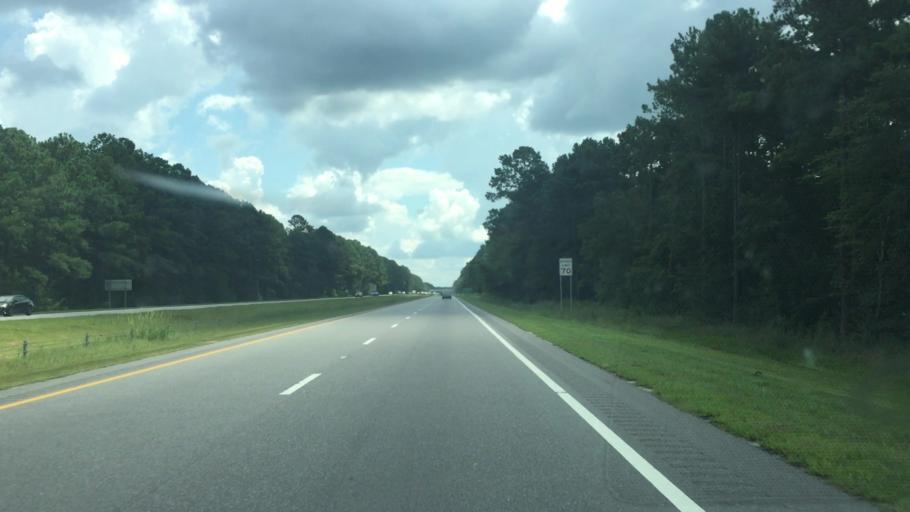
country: US
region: North Carolina
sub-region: Columbus County
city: Chadbourn
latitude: 34.3934
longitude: -78.8915
